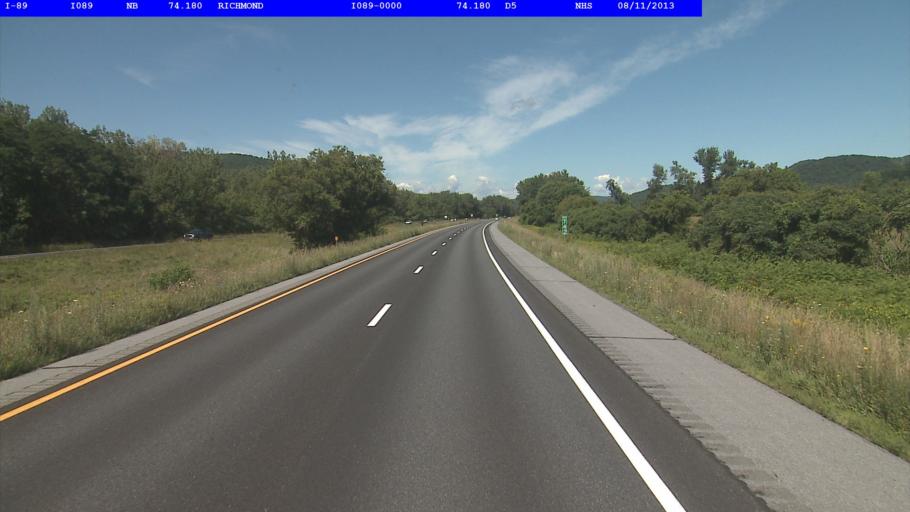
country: US
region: Vermont
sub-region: Chittenden County
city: Jericho
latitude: 44.3892
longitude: -72.9462
